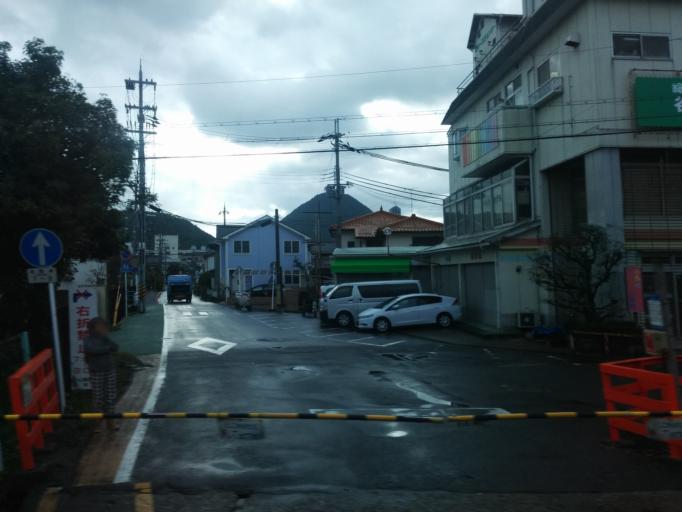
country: JP
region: Shiga Prefecture
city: Moriyama
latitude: 35.0664
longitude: 136.0198
